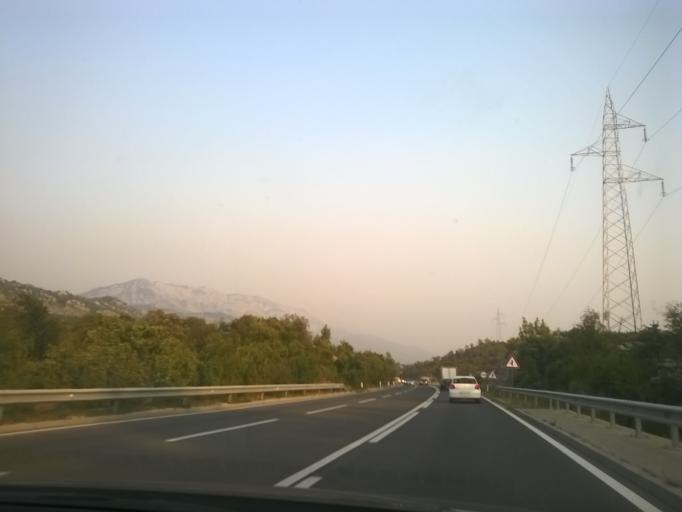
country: ME
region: Opstina Niksic
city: Niksic
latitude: 42.7101
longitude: 18.9532
